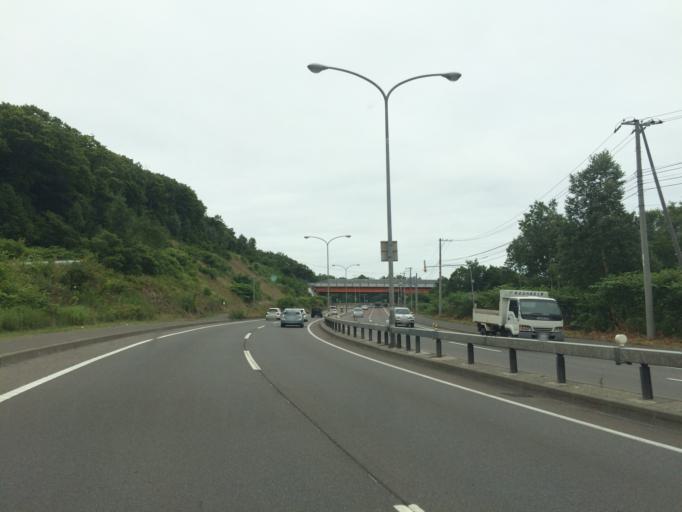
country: JP
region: Hokkaido
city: Otaru
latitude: 43.1545
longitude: 141.1096
